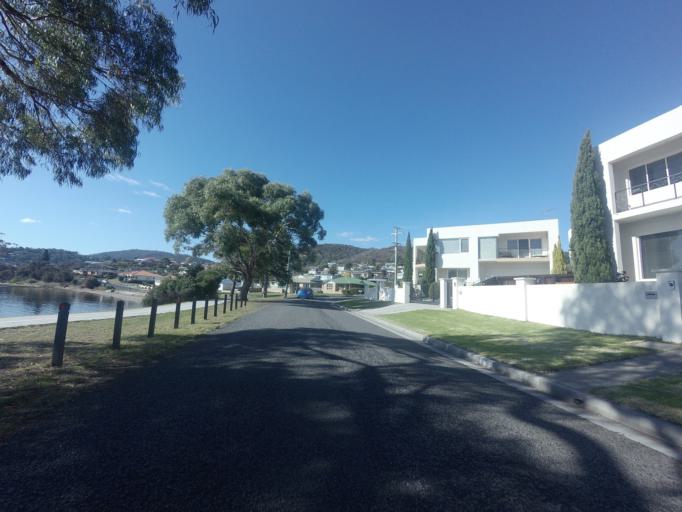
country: AU
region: Tasmania
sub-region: Clarence
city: Lindisfarne
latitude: -42.8580
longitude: 147.3539
